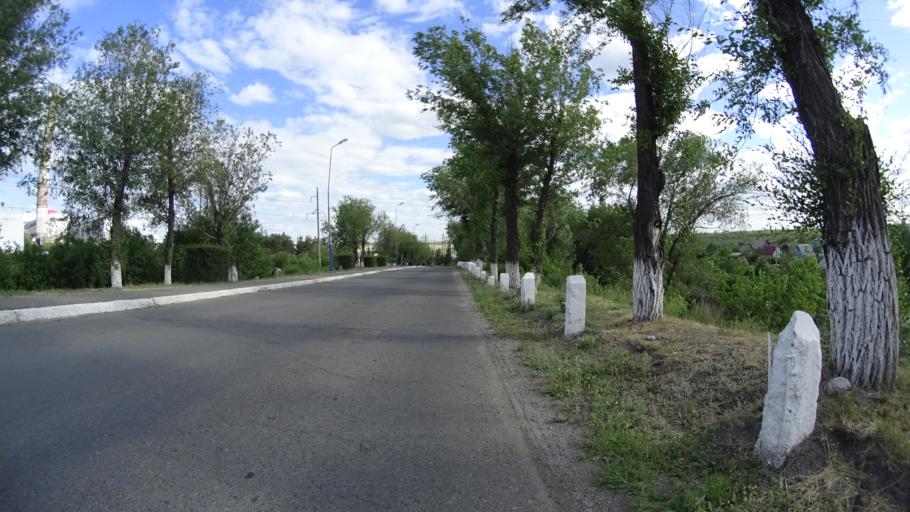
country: RU
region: Chelyabinsk
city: Troitsk
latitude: 54.0392
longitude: 61.6397
